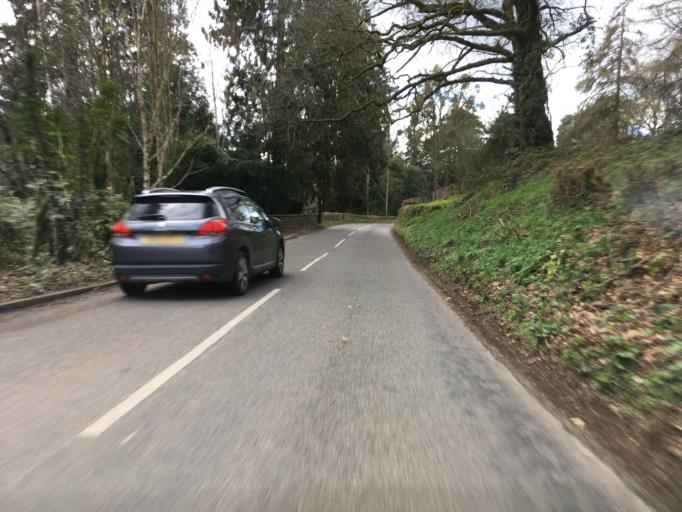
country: GB
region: Wales
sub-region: Monmouthshire
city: Tintern
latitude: 51.7456
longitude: -2.6517
